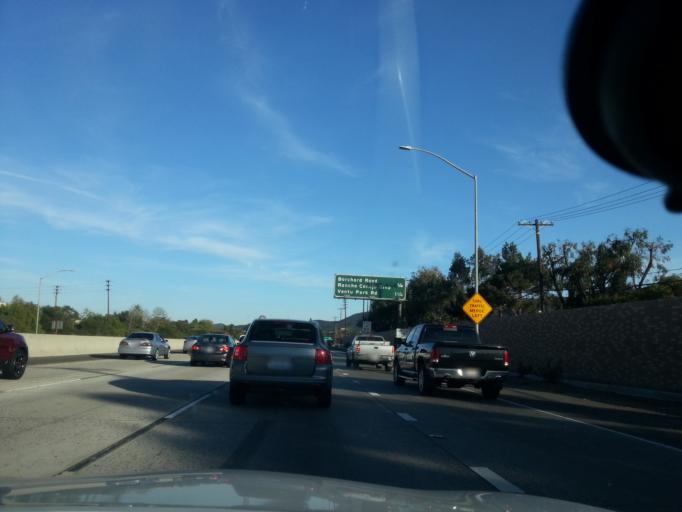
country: US
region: California
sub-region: Ventura County
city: Casa Conejo
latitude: 34.1879
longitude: -118.9351
